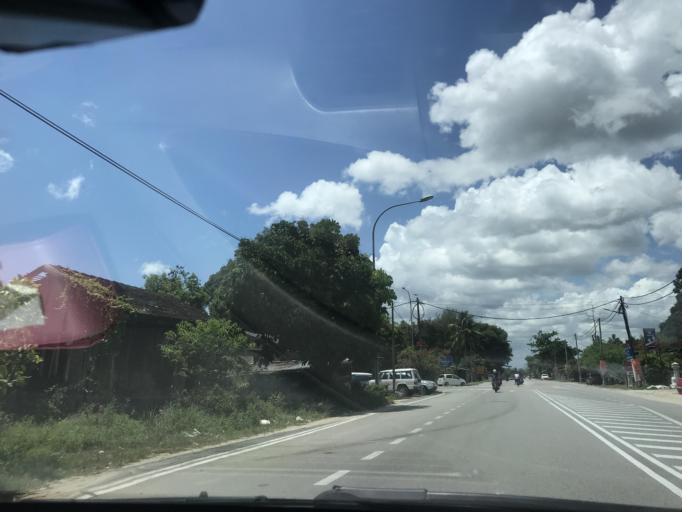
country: MY
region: Kelantan
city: Tumpat
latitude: 6.1919
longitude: 102.1524
